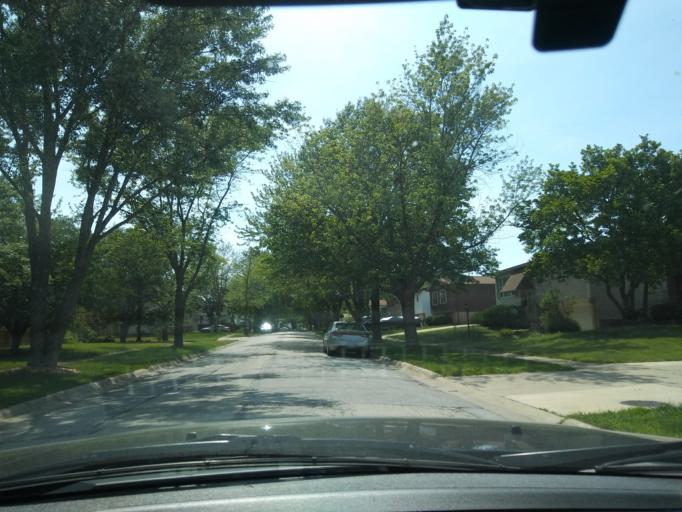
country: US
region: Illinois
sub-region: Cook County
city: Oak Forest
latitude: 41.6103
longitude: -87.7601
